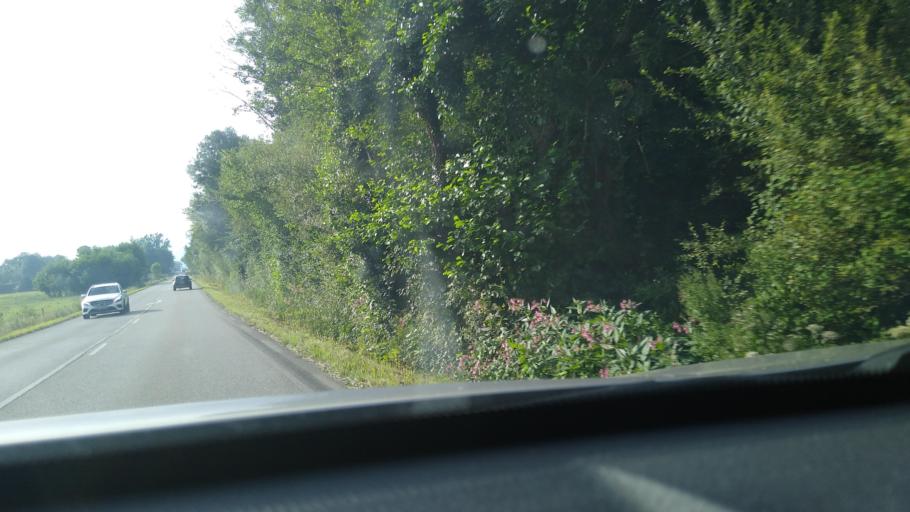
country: FR
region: Midi-Pyrenees
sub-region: Departement de l'Ariege
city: Saint-Lizier
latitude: 43.0264
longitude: 1.0894
